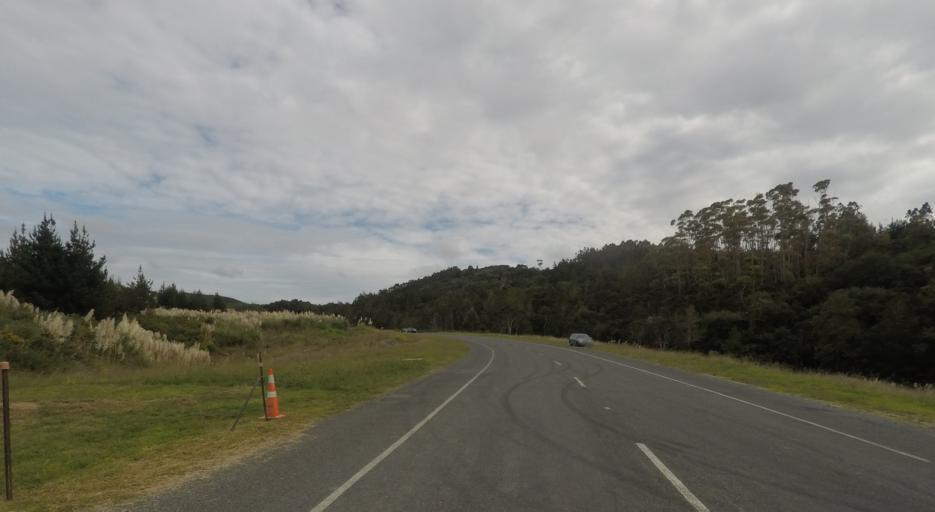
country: NZ
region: Auckland
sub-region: Auckland
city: Rothesay Bay
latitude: -36.6545
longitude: 174.7216
